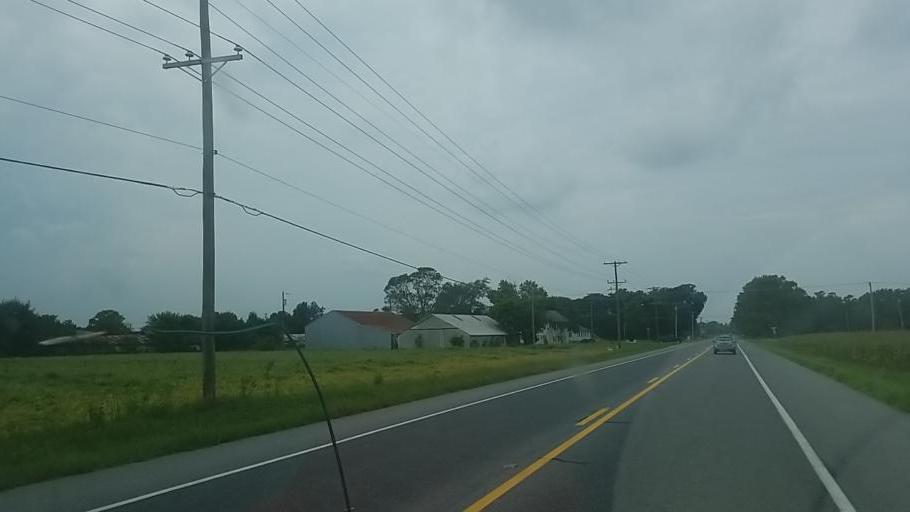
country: US
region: Delaware
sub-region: Sussex County
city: Long Neck
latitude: 38.5562
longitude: -75.1716
